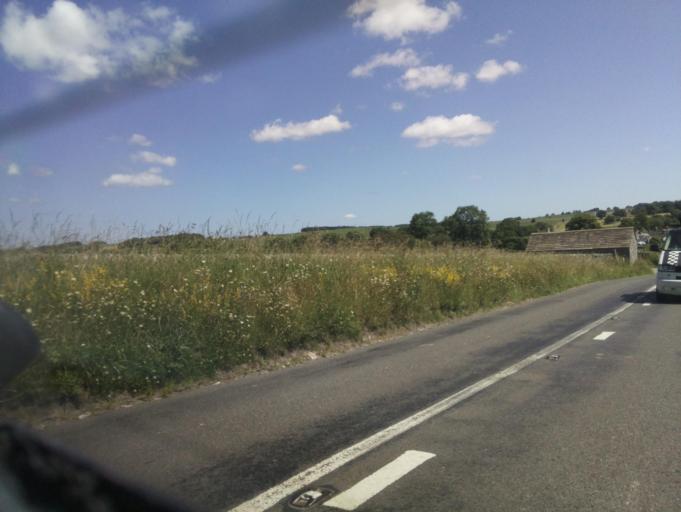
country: GB
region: England
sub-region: Derbyshire
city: Tideswell
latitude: 53.1958
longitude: -1.7821
